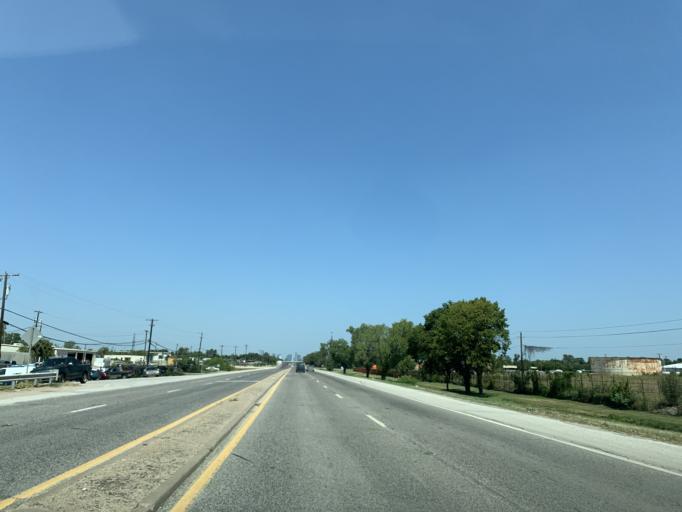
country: US
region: Texas
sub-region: Dallas County
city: Hutchins
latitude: 32.6932
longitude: -96.7410
